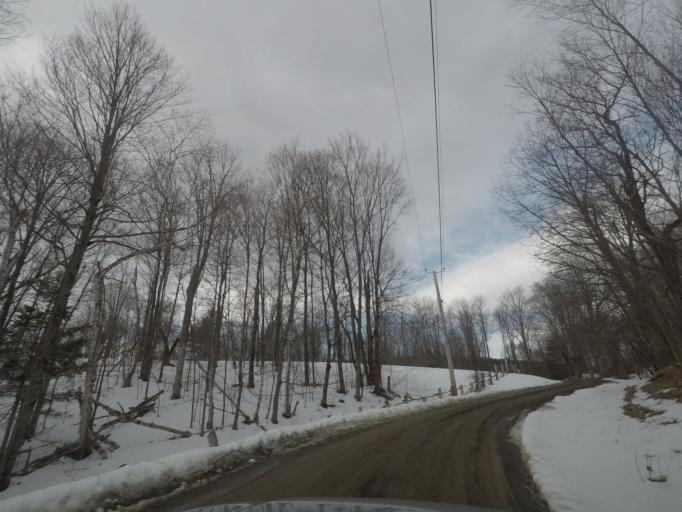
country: US
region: New York
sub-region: Saratoga County
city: Waterford
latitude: 42.7856
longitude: -73.6052
